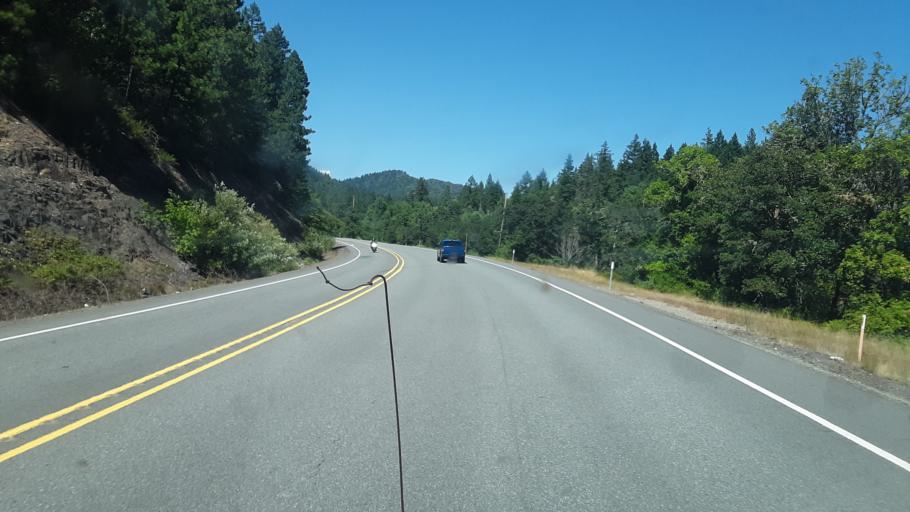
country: US
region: Oregon
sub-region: Josephine County
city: Redwood
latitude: 42.3722
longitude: -123.5013
